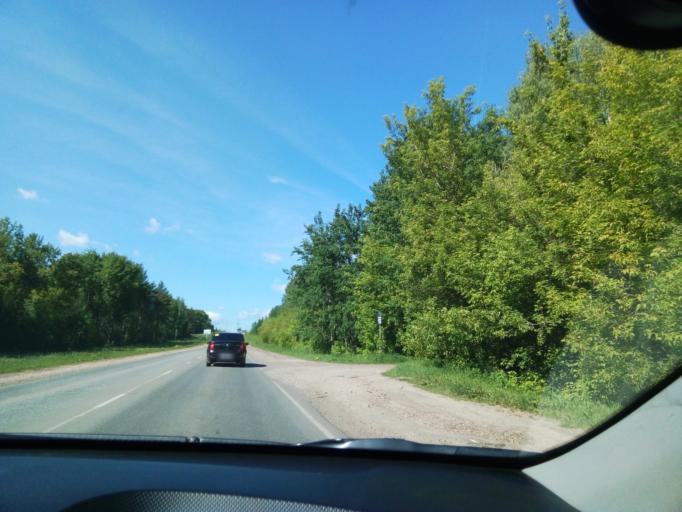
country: RU
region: Chuvashia
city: Novocheboksarsk
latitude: 56.0800
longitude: 47.5019
